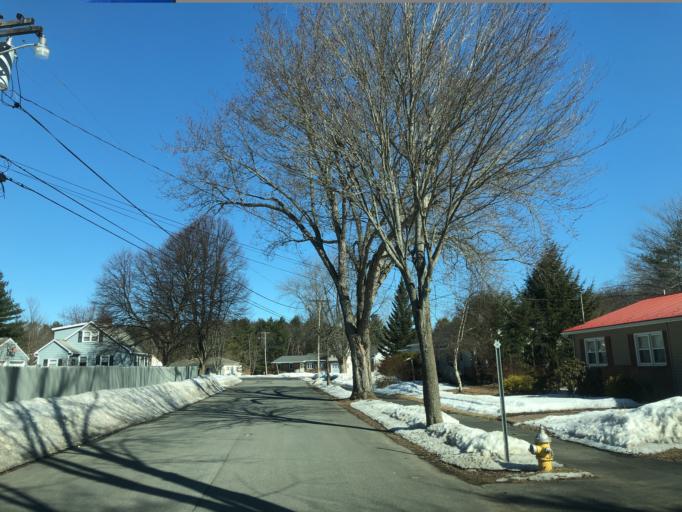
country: US
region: Maine
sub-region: Penobscot County
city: Brewer
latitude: 44.8200
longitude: -68.7538
